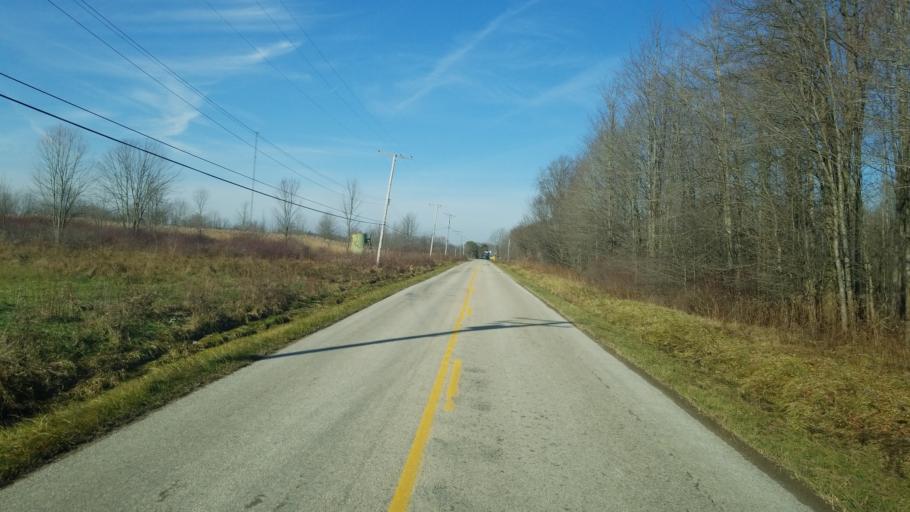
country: US
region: Ohio
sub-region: Ashtabula County
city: Jefferson
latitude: 41.7199
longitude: -80.6968
